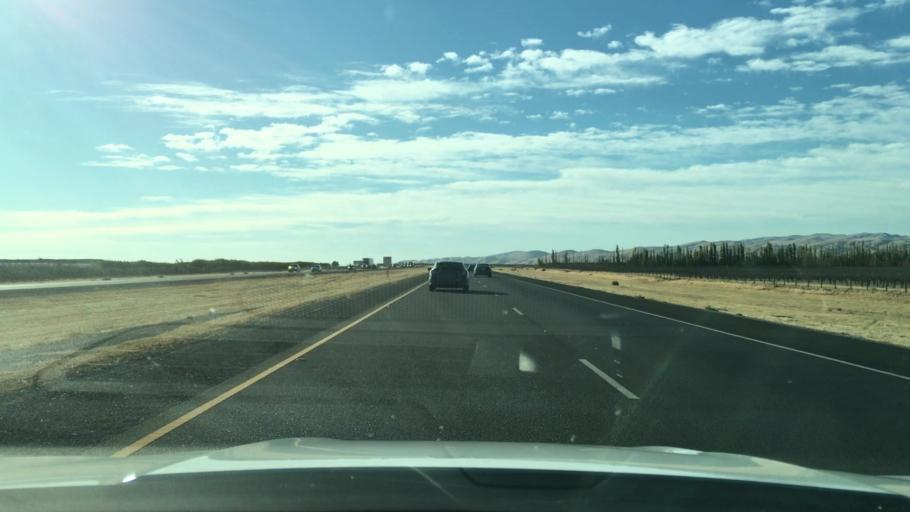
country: US
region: California
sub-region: Fresno County
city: Mendota
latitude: 36.6309
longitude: -120.6163
